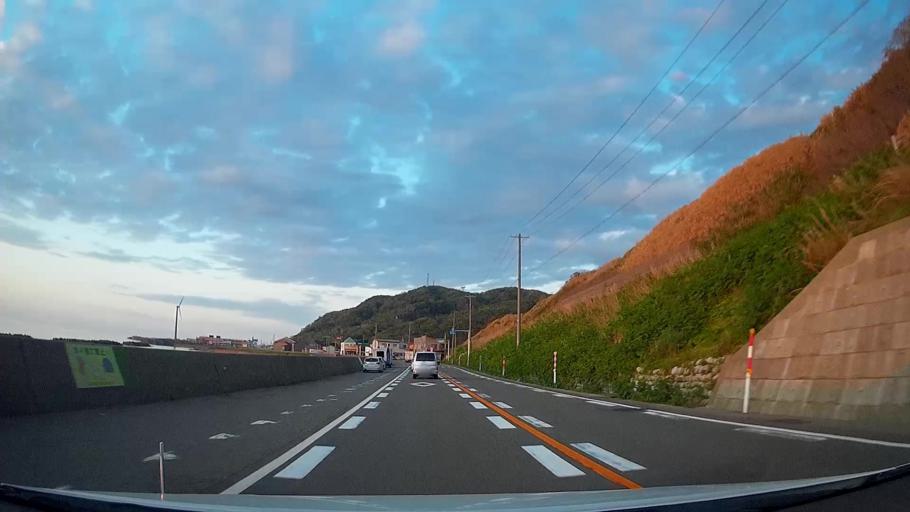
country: JP
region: Niigata
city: Joetsu
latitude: 37.1562
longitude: 138.0815
